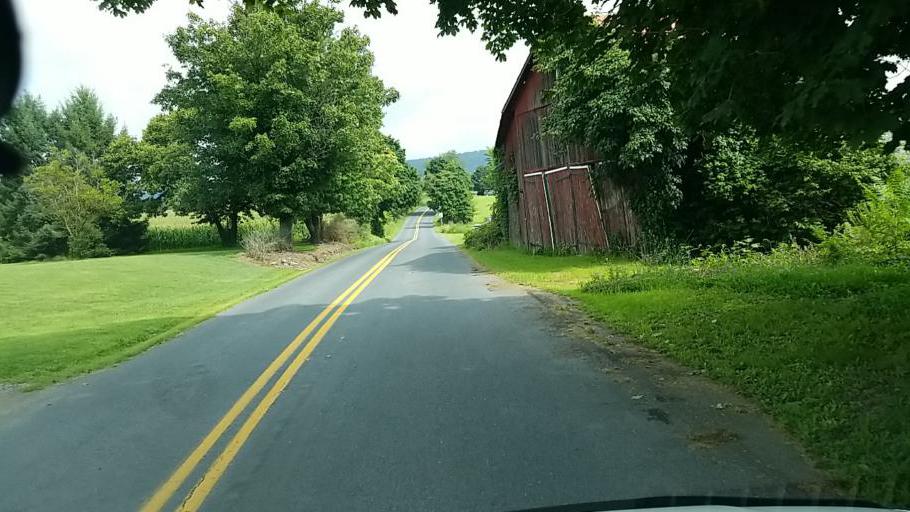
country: US
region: Pennsylvania
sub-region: Dauphin County
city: Matamoras
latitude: 40.5011
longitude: -76.8848
